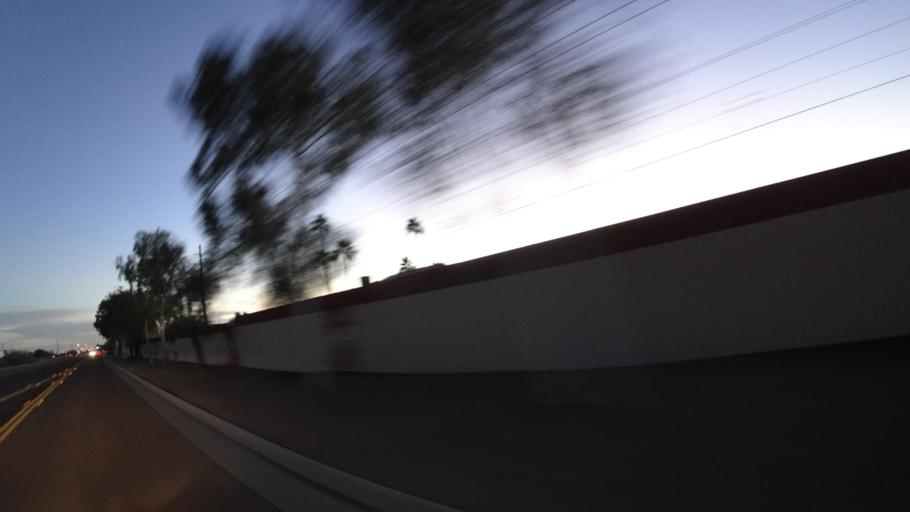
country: US
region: Arizona
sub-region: Maricopa County
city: Scottsdale
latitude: 33.4850
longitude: -111.8918
